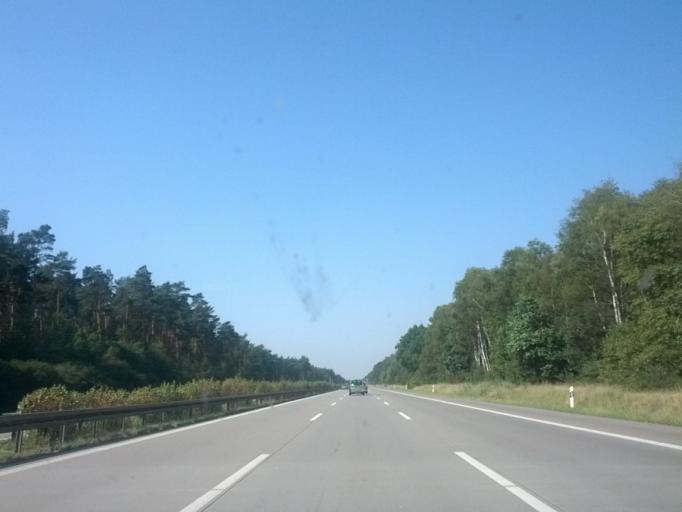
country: DE
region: Brandenburg
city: Wildau
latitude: 52.3192
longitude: 13.6905
